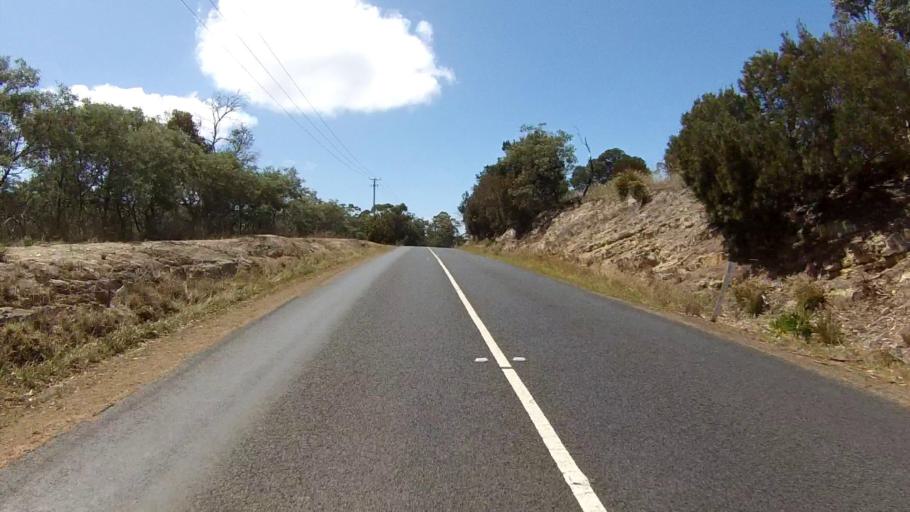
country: AU
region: Tasmania
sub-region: Clarence
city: Sandford
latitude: -42.9591
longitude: 147.4747
